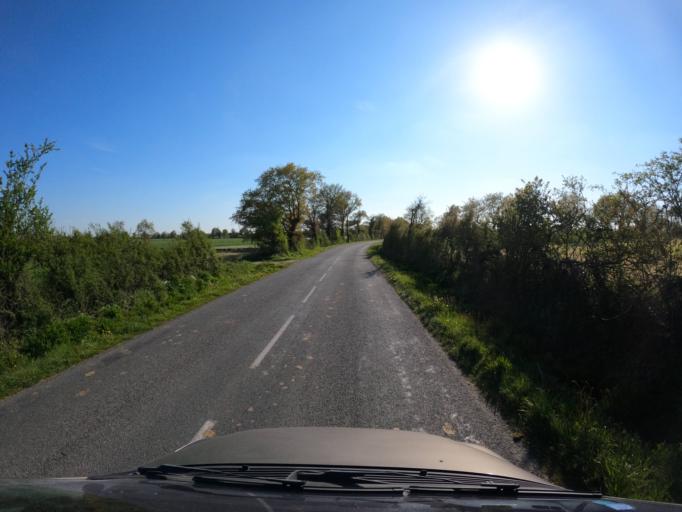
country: FR
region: Pays de la Loire
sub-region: Departement de la Vendee
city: Beaurepaire
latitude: 46.9297
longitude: -1.1056
